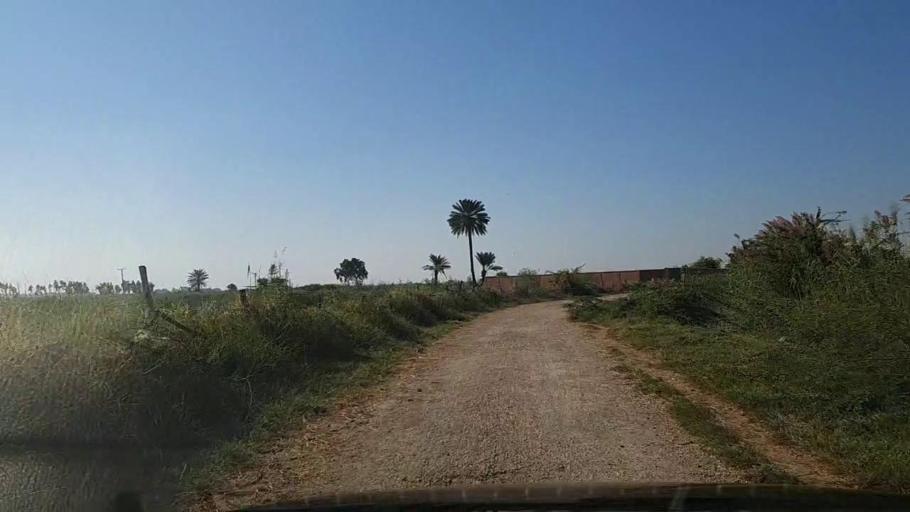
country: PK
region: Sindh
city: Thatta
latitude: 24.7042
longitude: 67.9081
